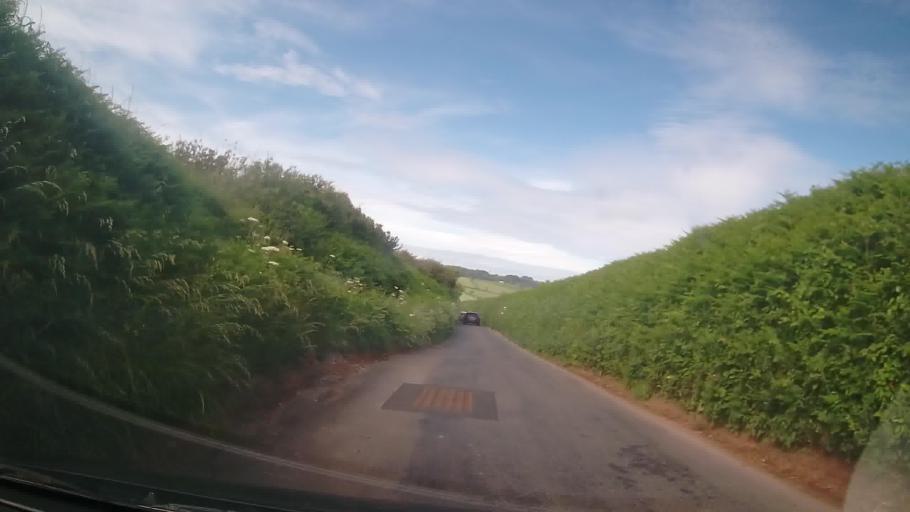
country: GB
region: England
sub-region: Devon
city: Salcombe
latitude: 50.2517
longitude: -3.6823
